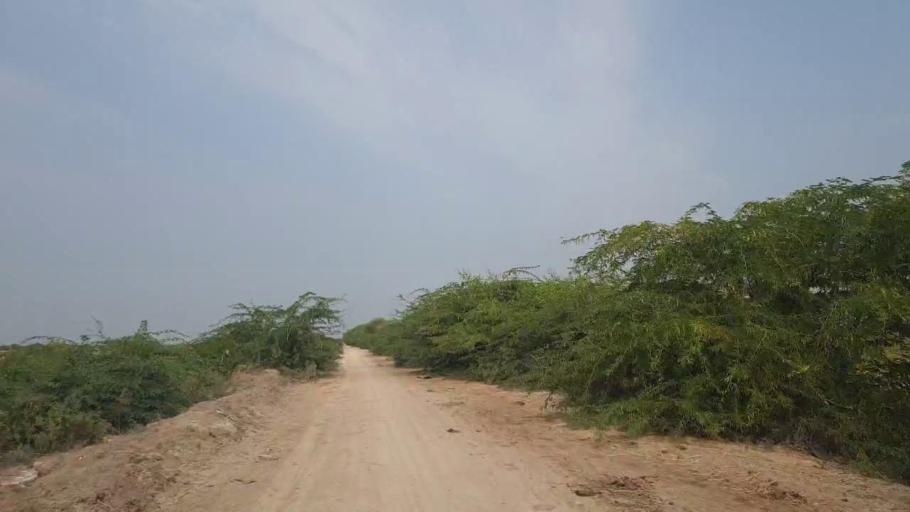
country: PK
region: Sindh
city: Badin
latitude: 24.5581
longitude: 68.7322
